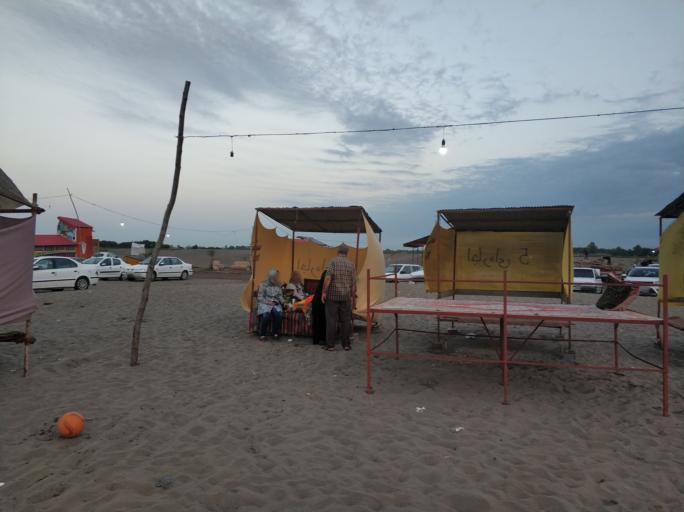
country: IR
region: Gilan
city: Astaneh-ye Ashrafiyeh
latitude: 37.4528
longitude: 49.8710
